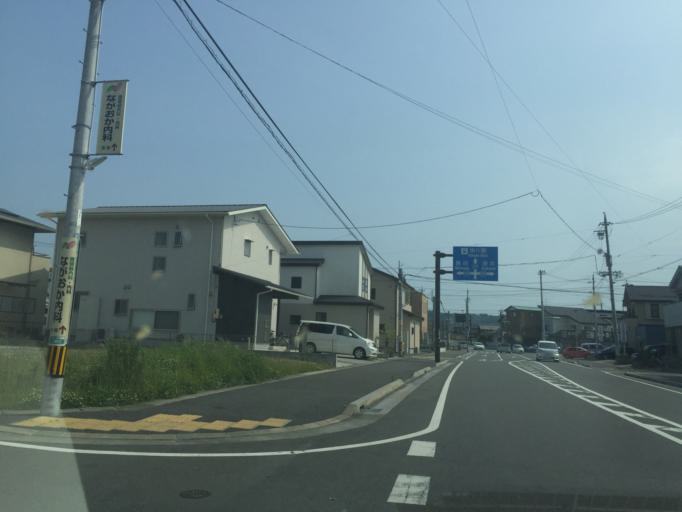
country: JP
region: Shizuoka
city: Kakegawa
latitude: 34.7776
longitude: 138.0018
